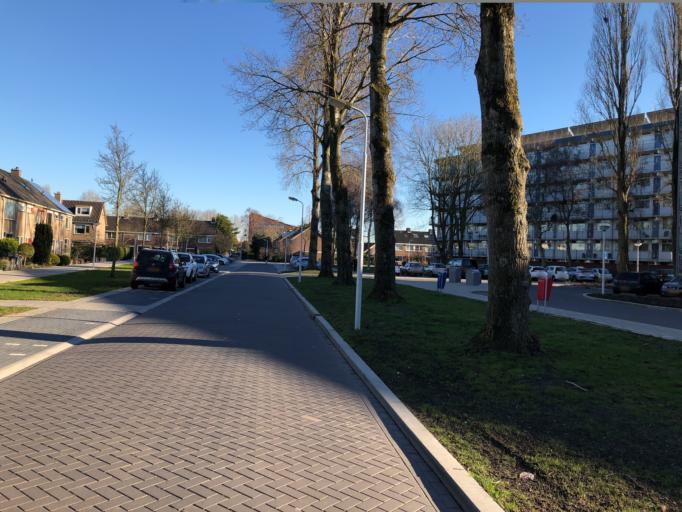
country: NL
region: North Holland
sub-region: Gemeente Uitgeest
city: Uitgeest
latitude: 52.5052
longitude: 4.7531
